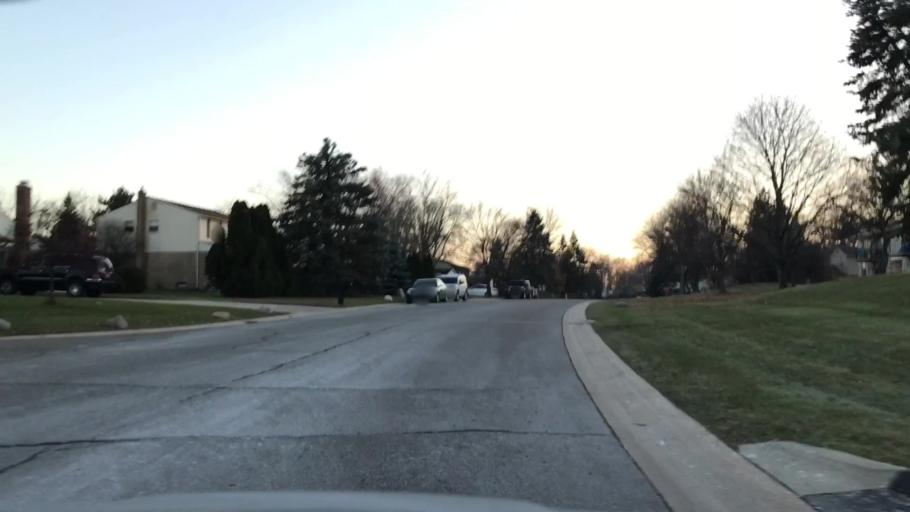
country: US
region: Michigan
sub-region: Wayne County
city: Northville
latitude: 42.4502
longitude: -83.4841
